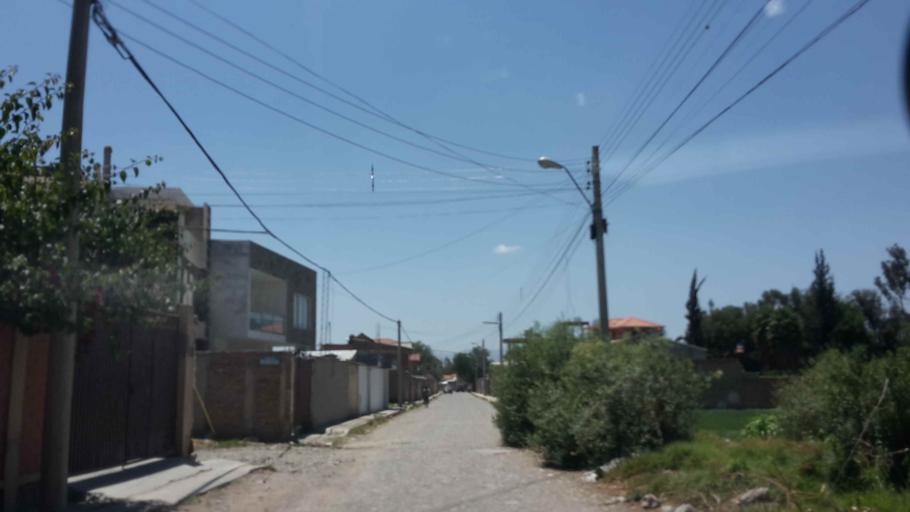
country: BO
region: Cochabamba
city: Cochabamba
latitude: -17.3649
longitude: -66.1974
